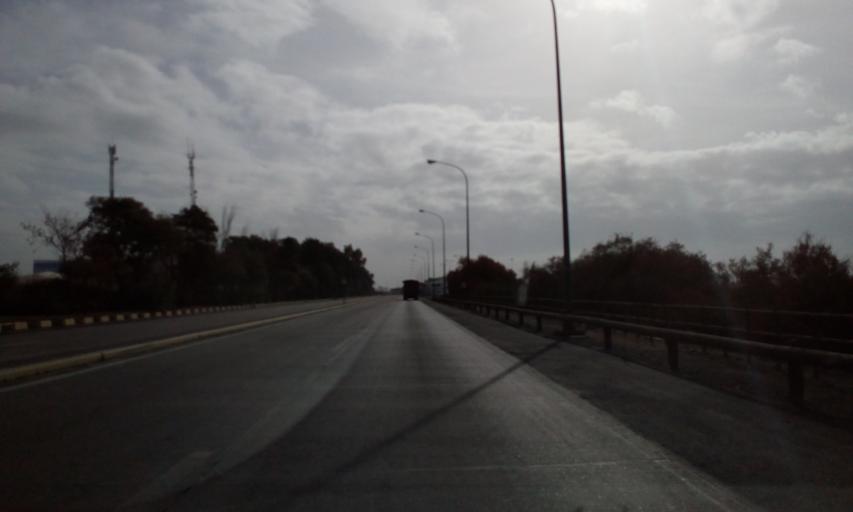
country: ES
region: Andalusia
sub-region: Provincia de Huelva
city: Punta Umbria
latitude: 37.2197
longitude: -6.9485
